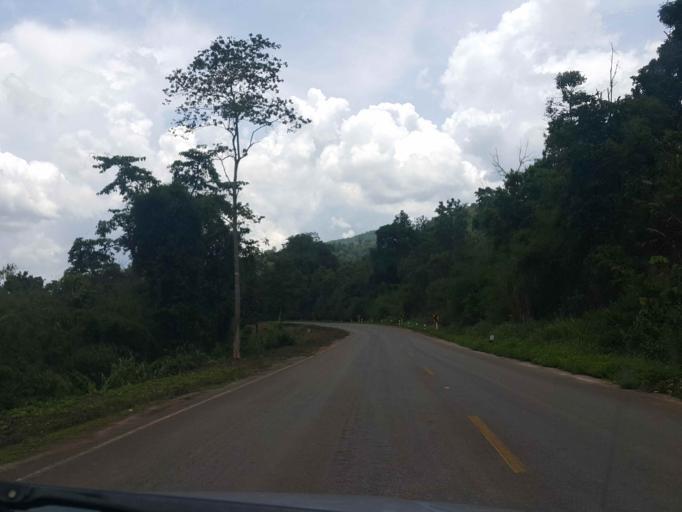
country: TH
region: Phayao
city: Chiang Muan
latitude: 18.9036
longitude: 100.1228
